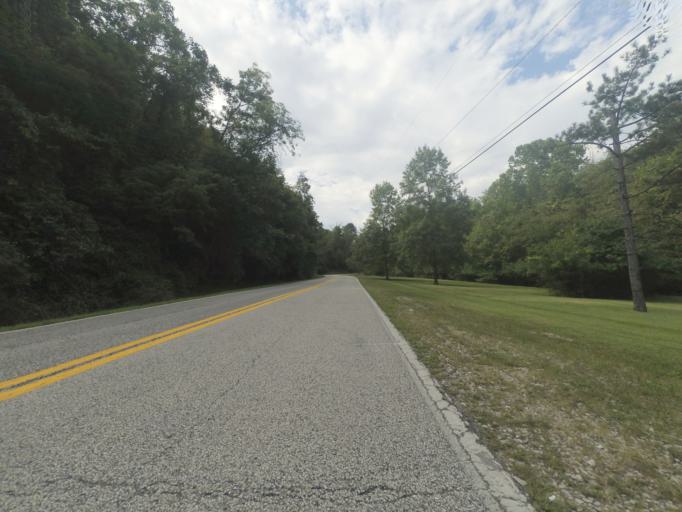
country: US
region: West Virginia
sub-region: Cabell County
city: Huntington
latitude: 38.3908
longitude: -82.4595
